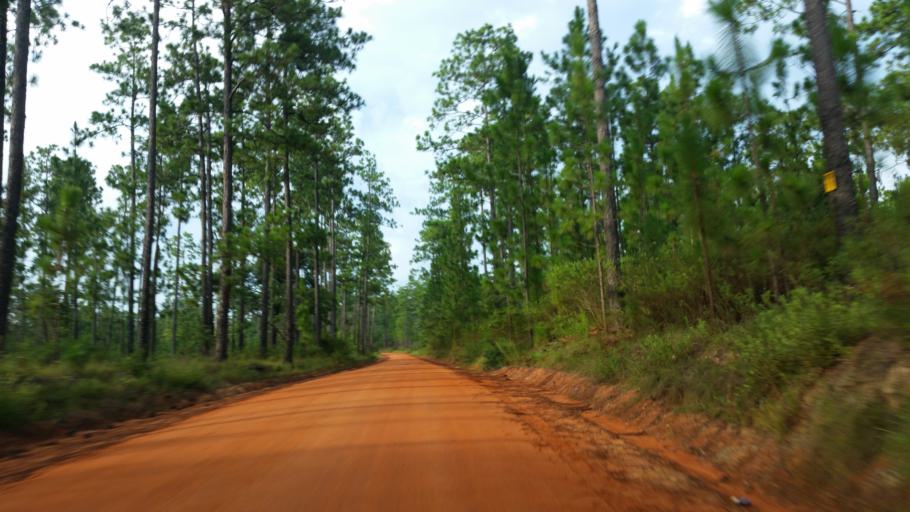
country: US
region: Alabama
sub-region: Escambia County
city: Atmore
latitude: 30.8810
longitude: -87.5826
